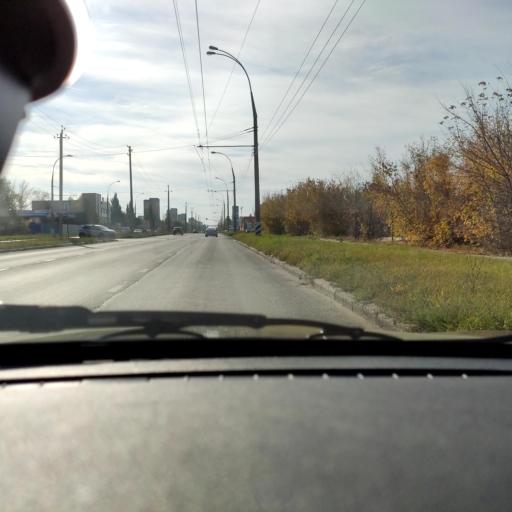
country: RU
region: Samara
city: Tol'yatti
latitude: 53.5418
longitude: 49.3003
